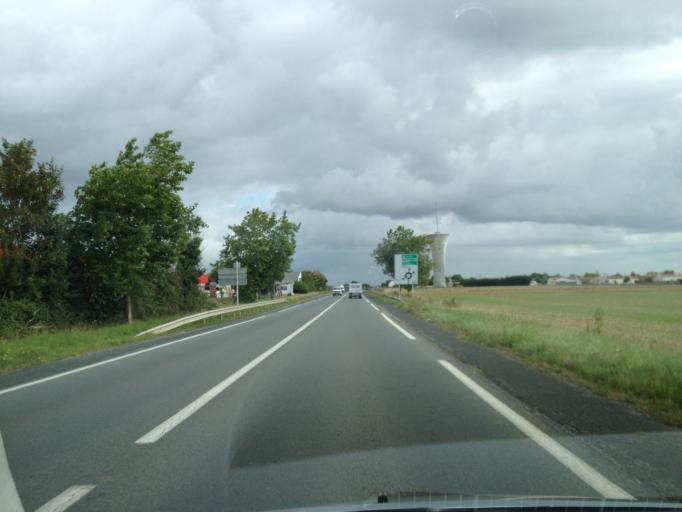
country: FR
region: Poitou-Charentes
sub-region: Departement de la Charente-Maritime
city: Andilly
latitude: 46.2584
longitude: -1.0113
